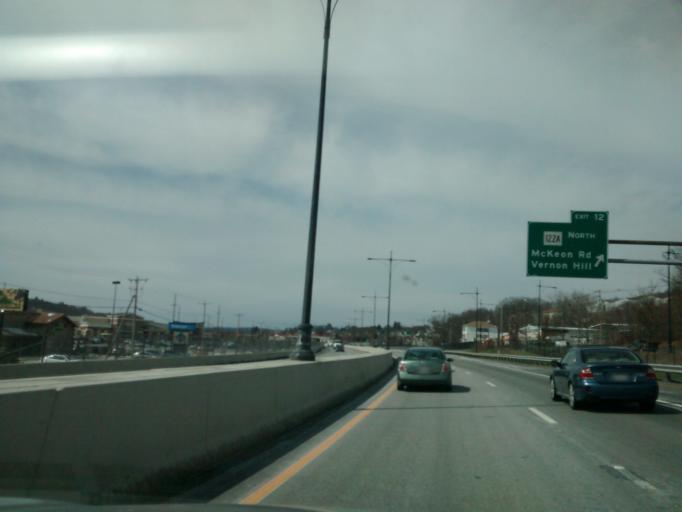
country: US
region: Massachusetts
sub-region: Worcester County
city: Sunderland
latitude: 42.2316
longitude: -71.7872
